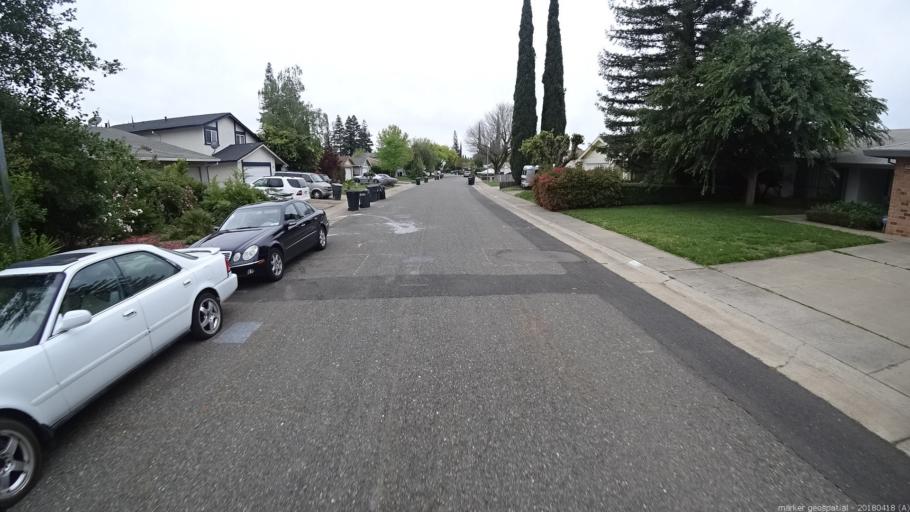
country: US
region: California
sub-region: Sacramento County
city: La Riviera
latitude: 38.5751
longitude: -121.3432
